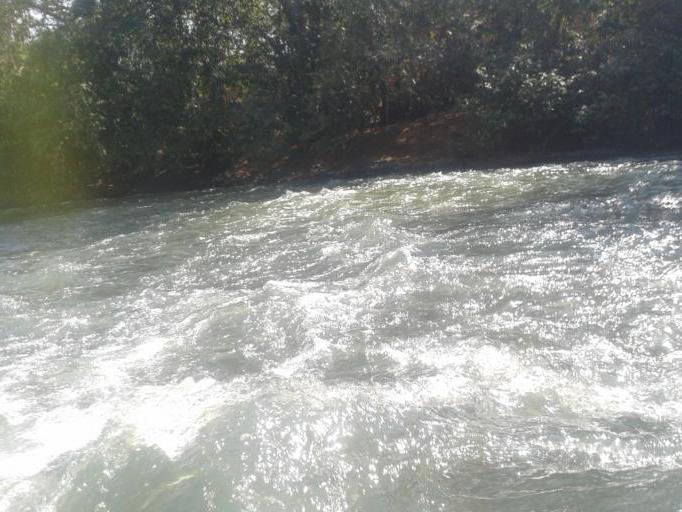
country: BR
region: Minas Gerais
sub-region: Ituiutaba
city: Ituiutaba
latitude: -18.9454
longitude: -49.4287
